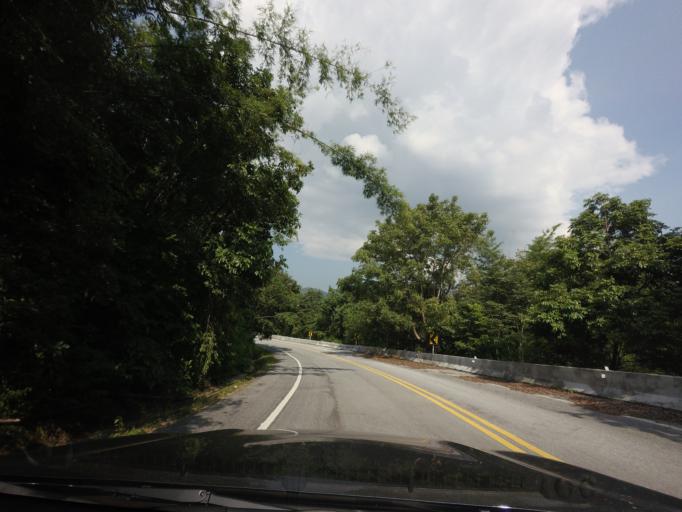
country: TH
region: Nan
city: Na Noi
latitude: 18.2766
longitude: 100.9697
